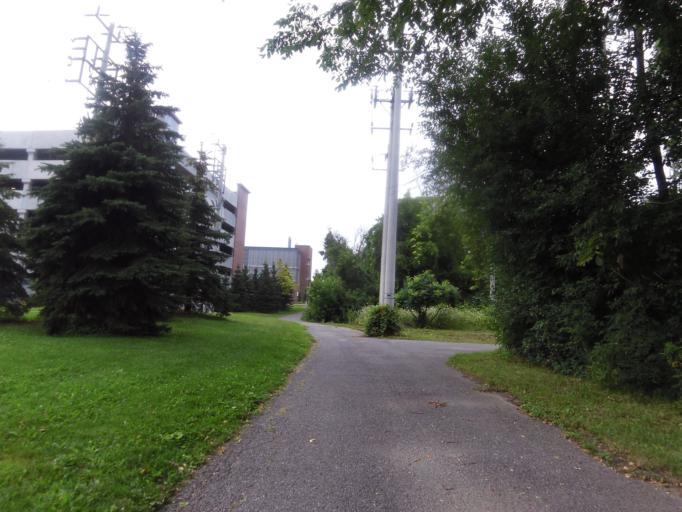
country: CA
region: Ontario
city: Bells Corners
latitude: 45.3361
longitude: -75.8101
